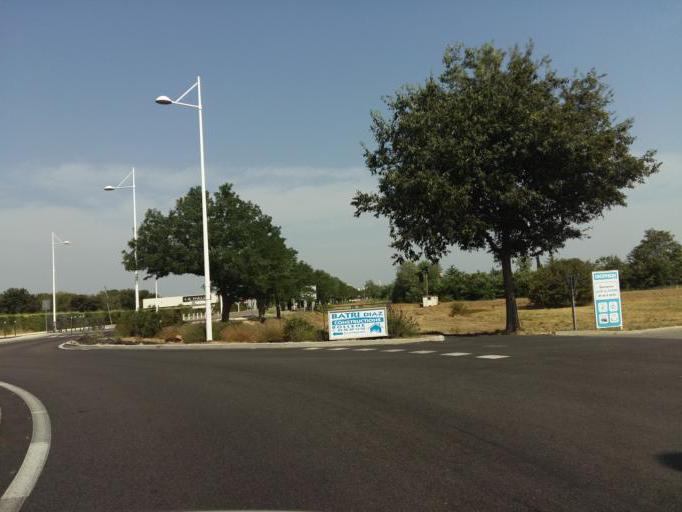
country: FR
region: Provence-Alpes-Cote d'Azur
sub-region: Departement du Vaucluse
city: Bollene
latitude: 44.2987
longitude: 4.7502
